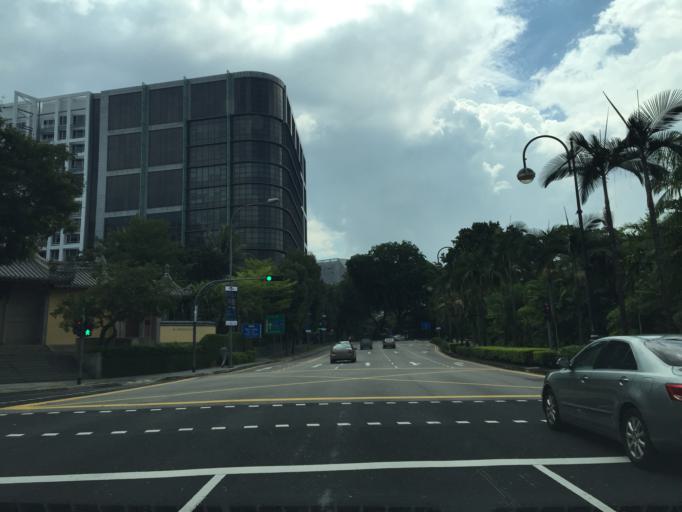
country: SG
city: Singapore
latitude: 1.2988
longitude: 103.8439
